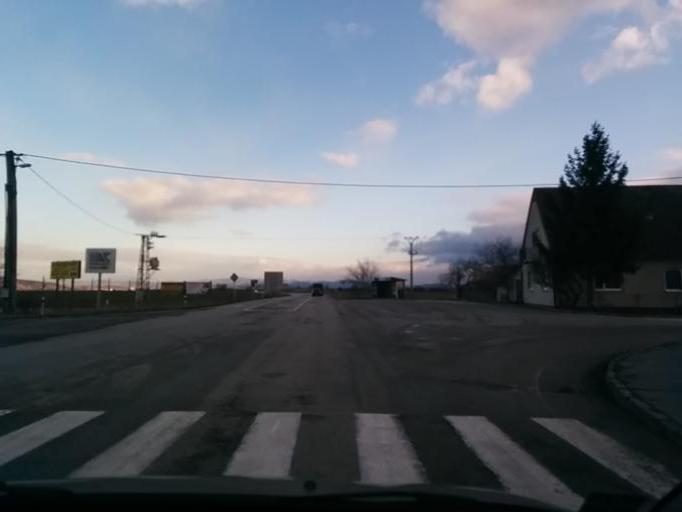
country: SK
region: Trnavsky
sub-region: Okres Trnava
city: Piestany
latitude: 48.6599
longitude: 17.8417
